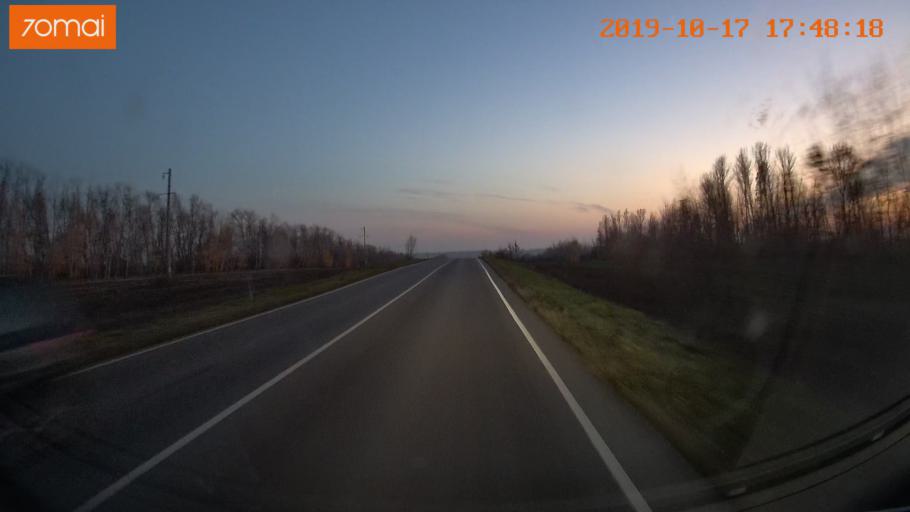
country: RU
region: Tula
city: Yepifan'
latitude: 53.6944
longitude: 38.6955
